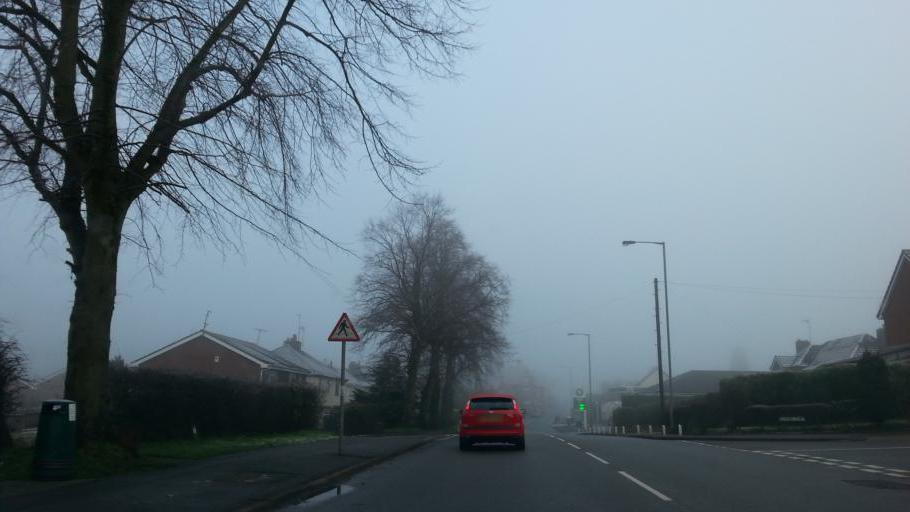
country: GB
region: England
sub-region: Staffordshire
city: Biddulph
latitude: 53.1219
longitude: -2.1696
